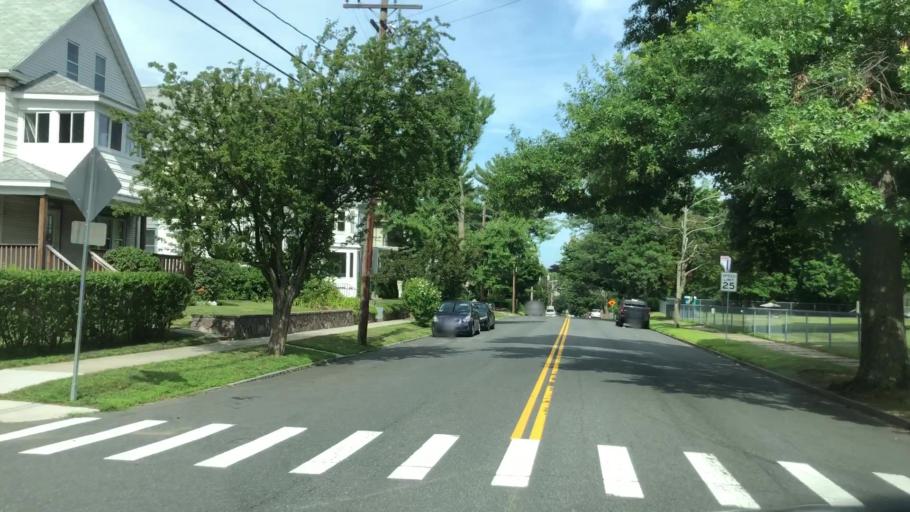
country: US
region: Massachusetts
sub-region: Hampden County
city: Holyoke
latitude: 42.2054
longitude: -72.6286
